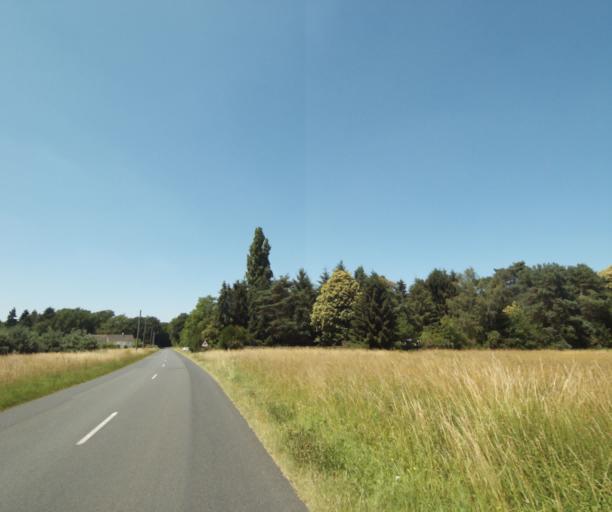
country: FR
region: Ile-de-France
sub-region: Departement de Seine-et-Marne
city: Noisy-sur-Ecole
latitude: 48.3687
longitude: 2.5133
